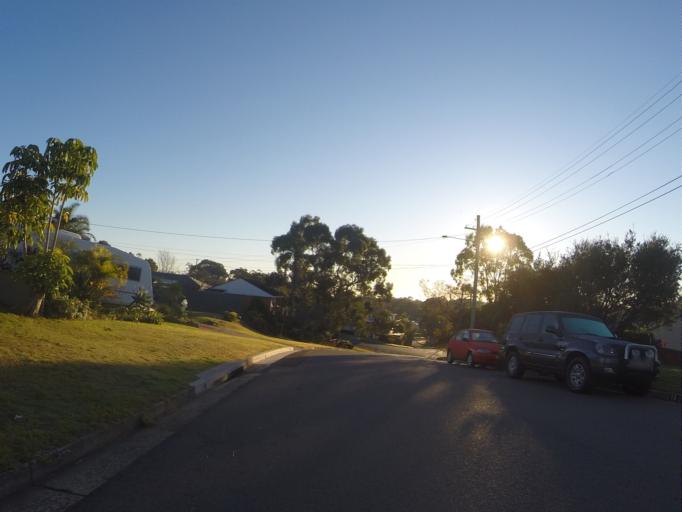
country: AU
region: New South Wales
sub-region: Sutherland Shire
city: Engadine
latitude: -34.0537
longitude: 151.0080
